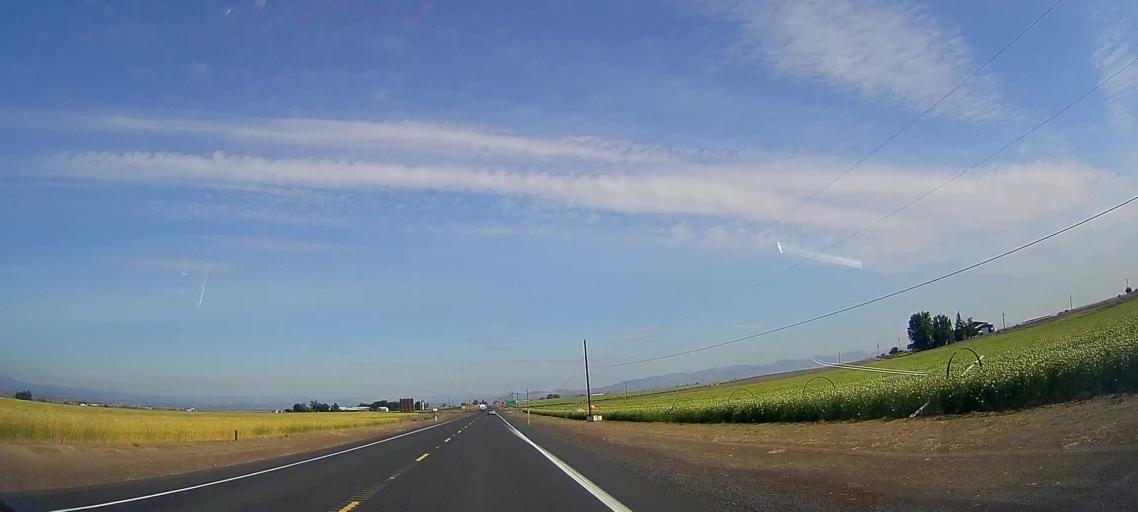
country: US
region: Oregon
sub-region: Jefferson County
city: Madras
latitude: 44.6762
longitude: -121.1442
